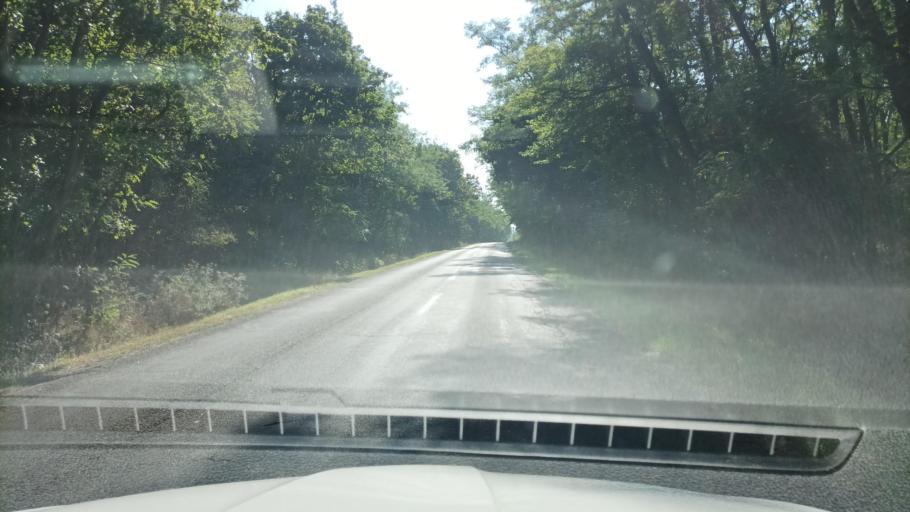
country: HU
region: Pest
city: Isaszeg
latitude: 47.5717
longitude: 19.4391
